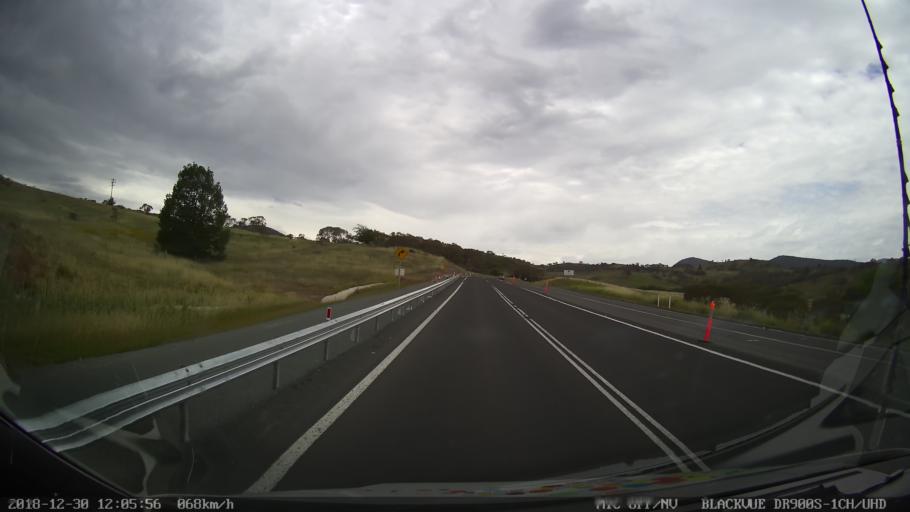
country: AU
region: New South Wales
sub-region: Snowy River
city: Jindabyne
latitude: -36.4130
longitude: 148.5997
